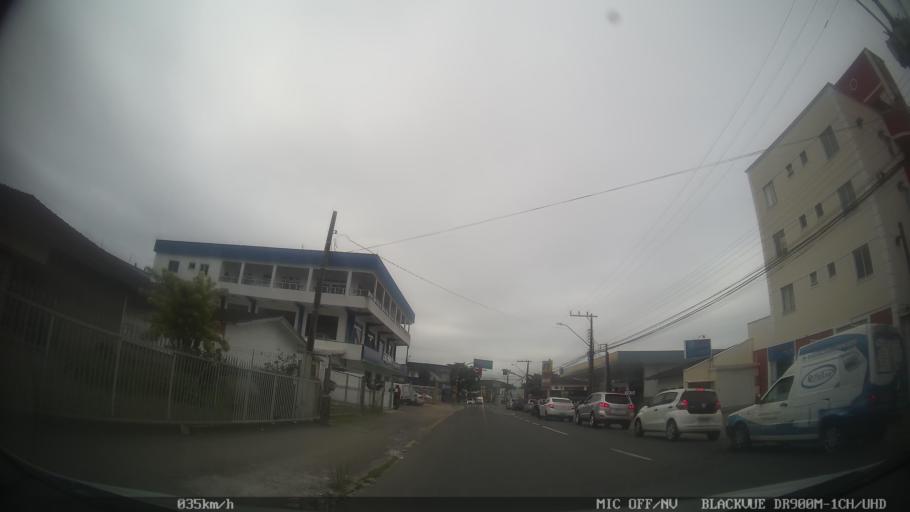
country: BR
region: Santa Catarina
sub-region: Joinville
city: Joinville
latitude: -26.3241
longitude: -48.8430
